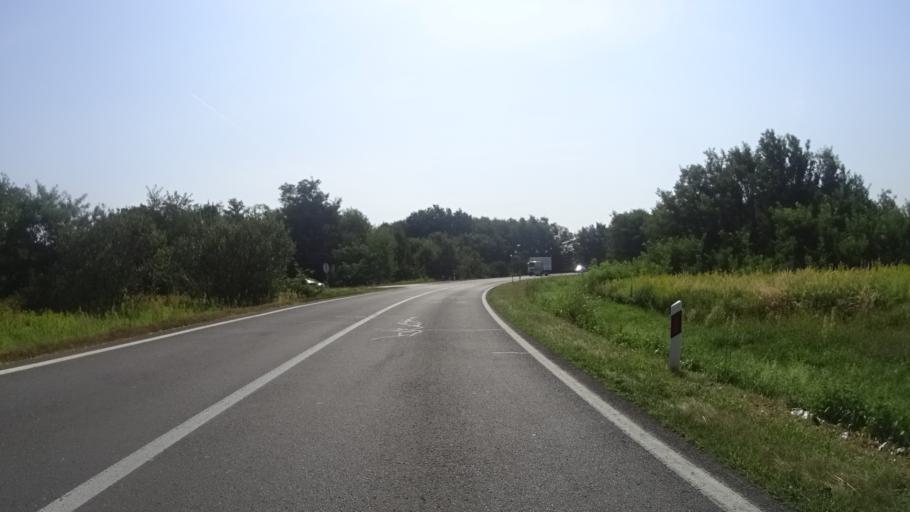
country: HR
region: Medimurska
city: Palovec
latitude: 46.3869
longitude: 16.5655
